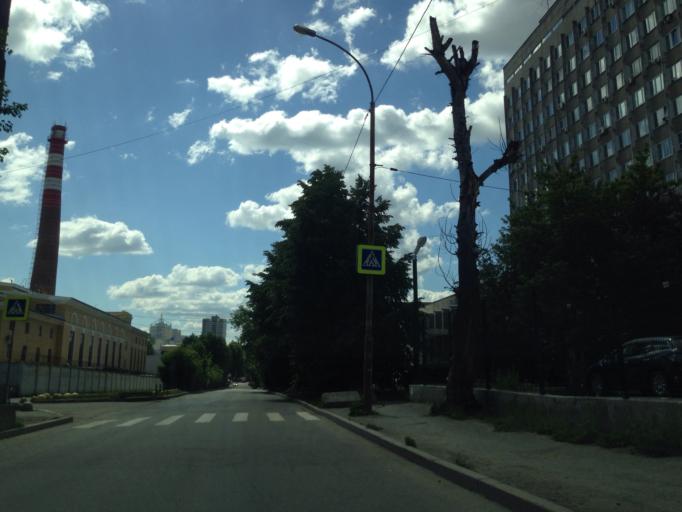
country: RU
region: Sverdlovsk
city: Yekaterinburg
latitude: 56.8436
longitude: 60.6557
